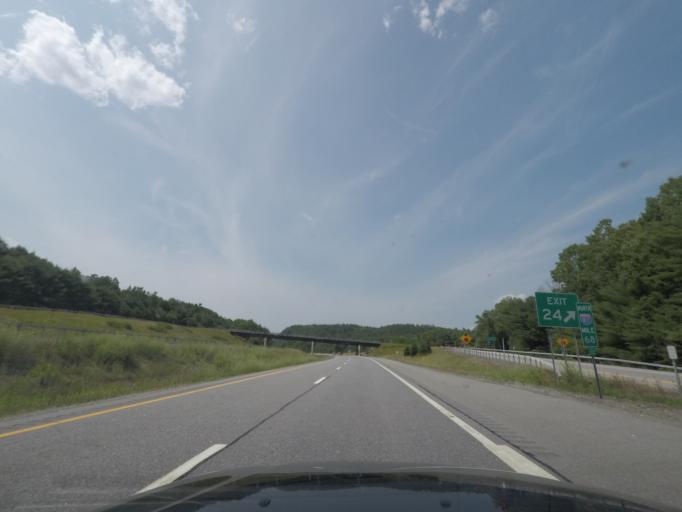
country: US
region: New York
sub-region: Warren County
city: Warrensburg
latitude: 43.6023
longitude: -73.7300
